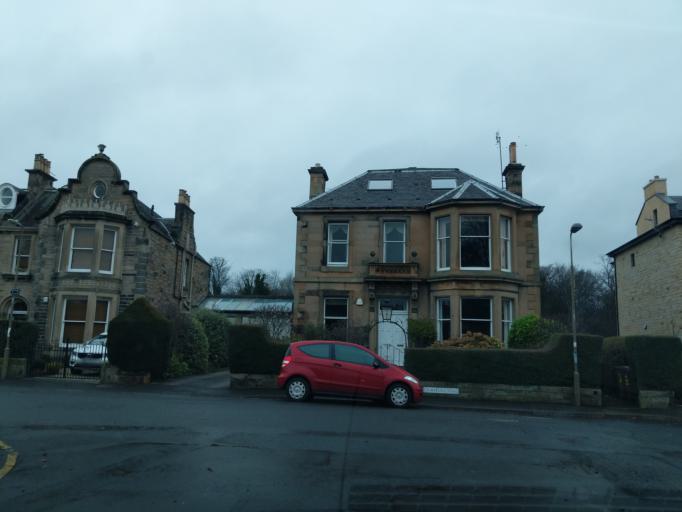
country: GB
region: Scotland
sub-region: Edinburgh
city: Edinburgh
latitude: 55.9308
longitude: -3.1681
